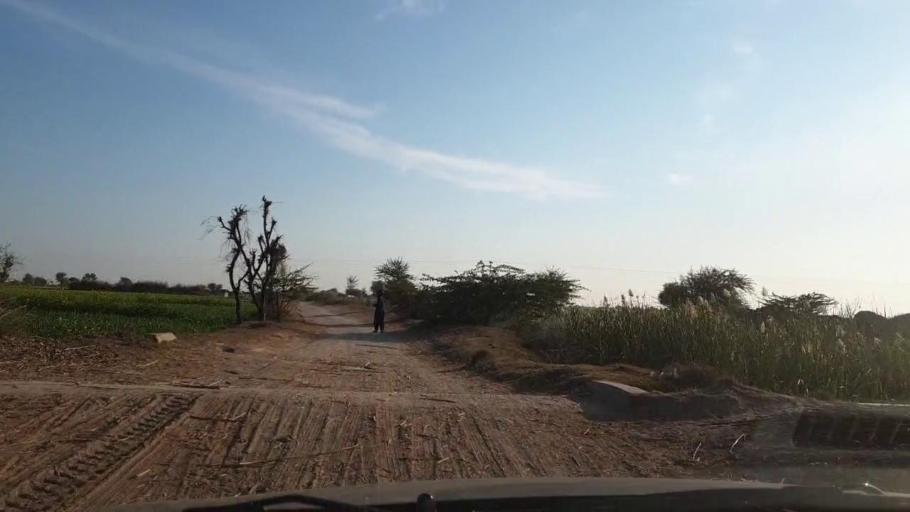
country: PK
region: Sindh
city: Khadro
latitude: 26.2194
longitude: 68.7405
